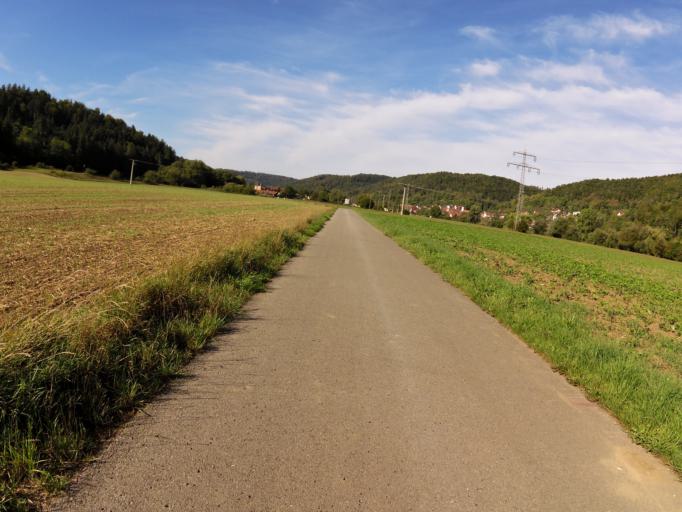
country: DE
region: Baden-Wuerttemberg
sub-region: Tuebingen Region
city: Hirrlingen
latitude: 48.4524
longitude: 8.8683
